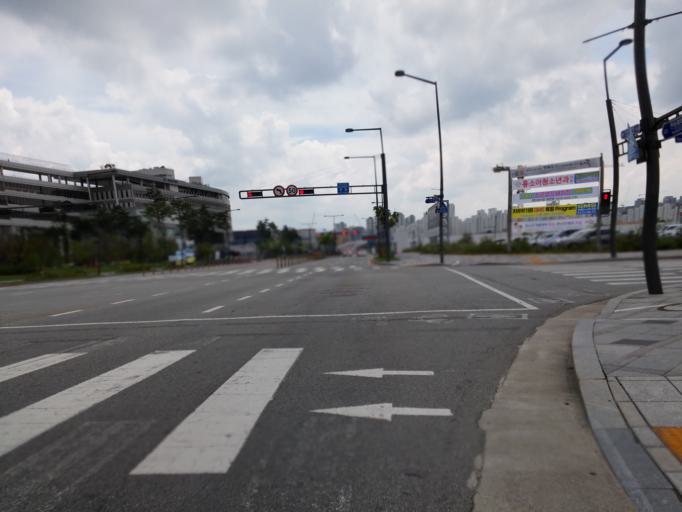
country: KR
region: Daejeon
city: Songgang-dong
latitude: 36.5027
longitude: 127.2603
